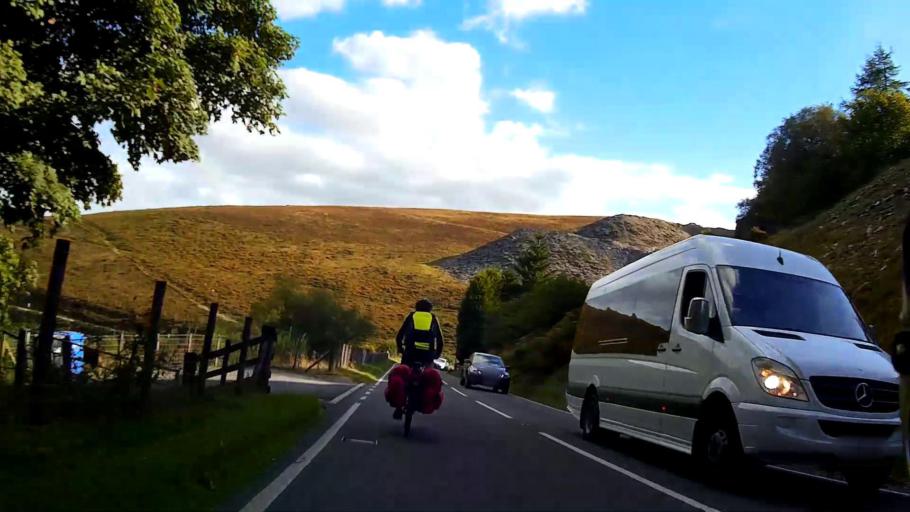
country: GB
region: Wales
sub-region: Denbighshire
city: Llandegla
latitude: 53.0130
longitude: -3.2159
